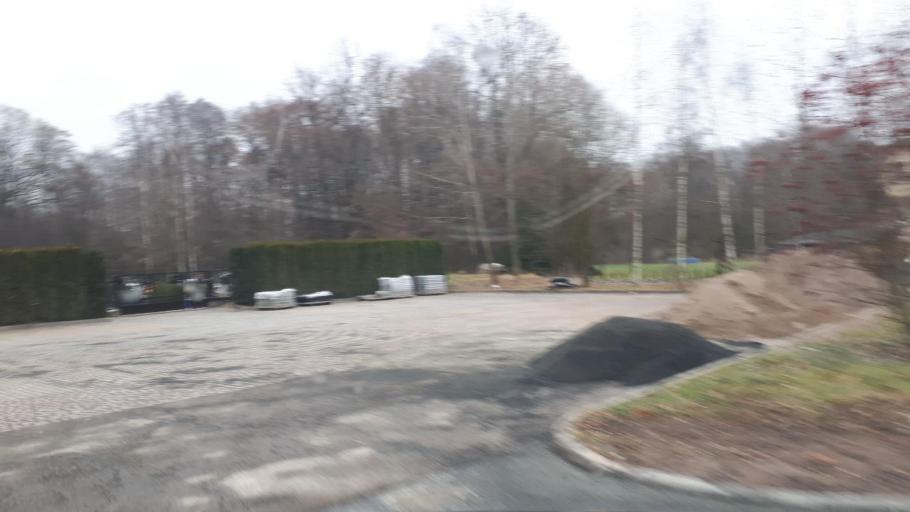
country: PL
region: Silesian Voivodeship
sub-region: Powiat bielski
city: Wilamowice
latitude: 49.9240
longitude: 19.1123
